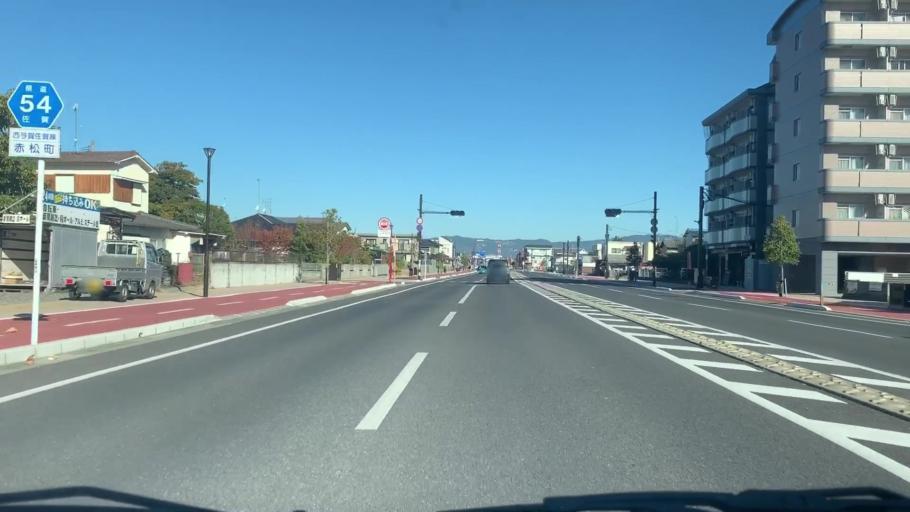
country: JP
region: Saga Prefecture
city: Saga-shi
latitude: 33.2462
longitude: 130.2931
